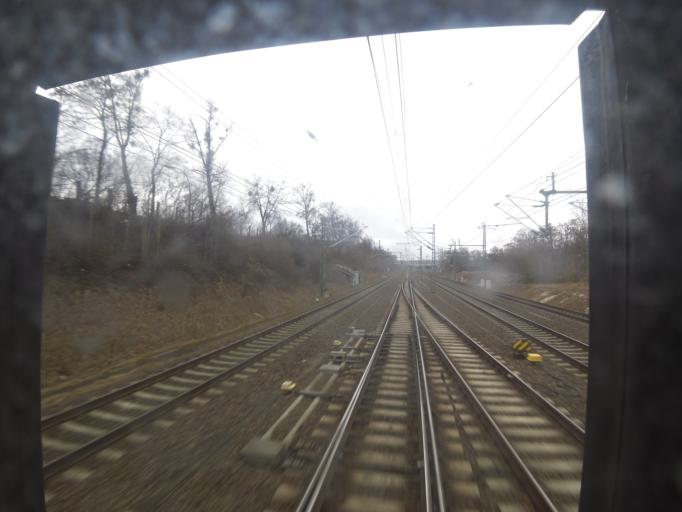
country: DE
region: Berlin
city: Berlin Schoeneberg
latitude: 52.4835
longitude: 13.3704
